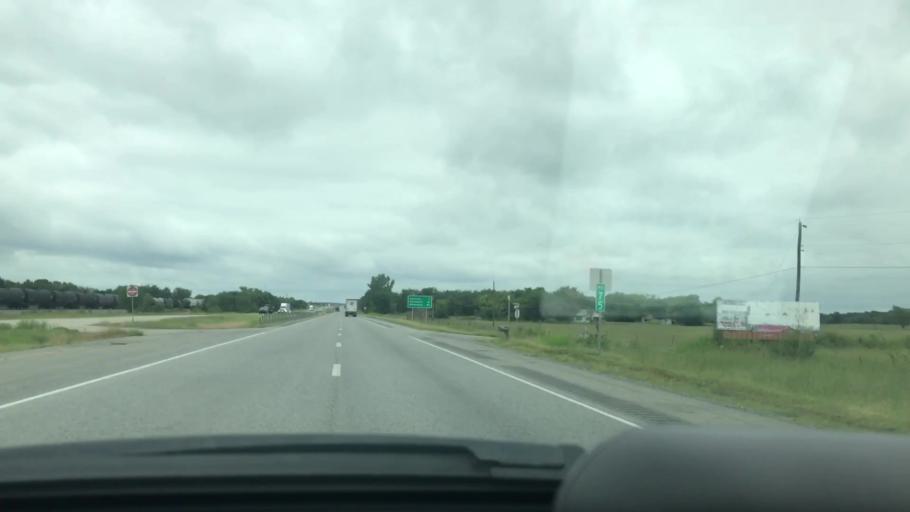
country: US
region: Oklahoma
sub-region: Pittsburg County
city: McAlester
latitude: 34.7382
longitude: -95.8989
